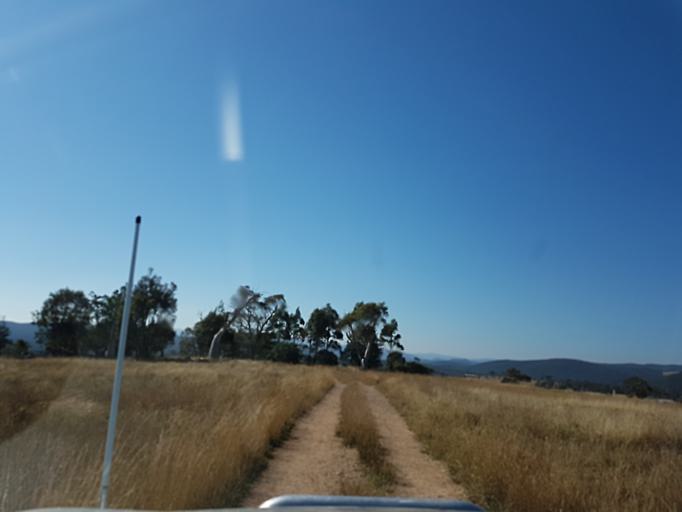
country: AU
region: New South Wales
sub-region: Snowy River
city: Jindabyne
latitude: -37.0482
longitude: 148.2890
